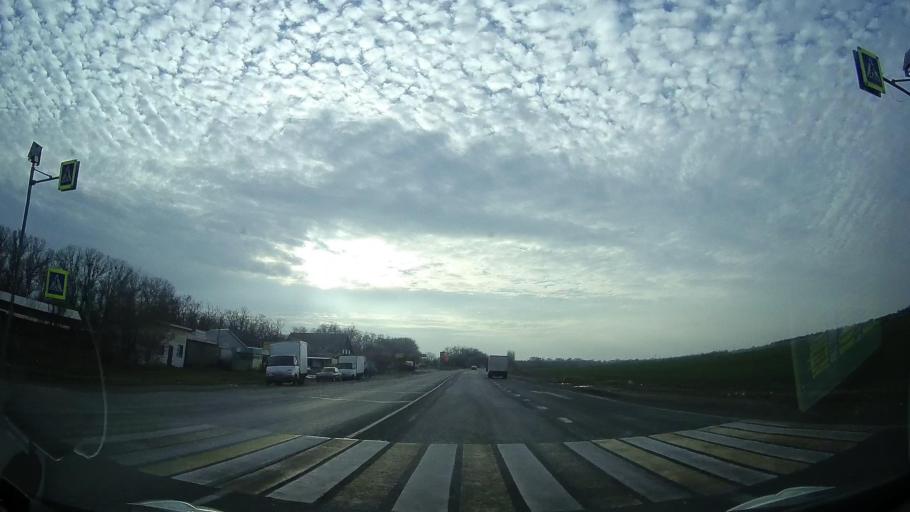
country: RU
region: Rostov
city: Bagayevskaya
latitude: 47.1653
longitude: 40.2670
